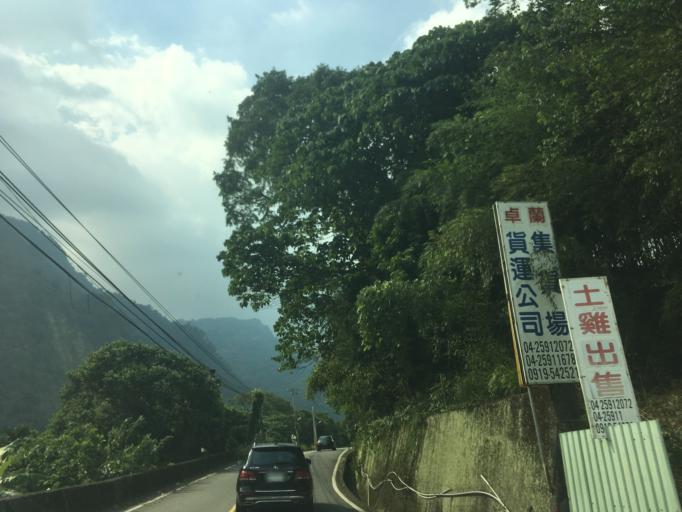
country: TW
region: Taiwan
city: Fengyuan
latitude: 24.3087
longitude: 120.9233
